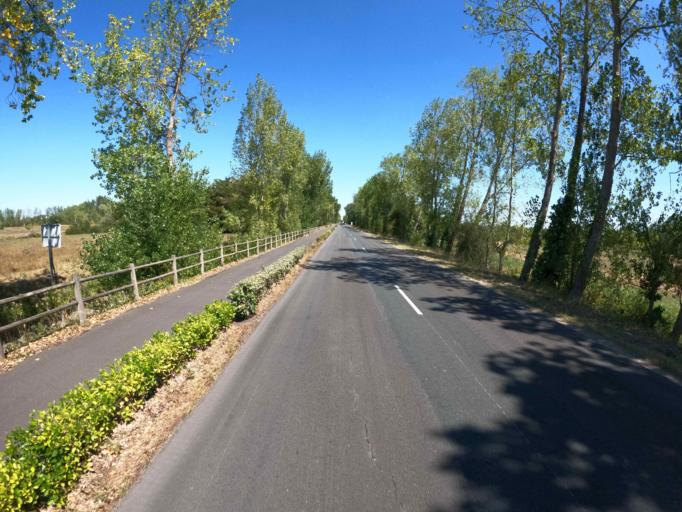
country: FR
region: Pays de la Loire
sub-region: Departement de la Vendee
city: Le Perrier
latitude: 46.8143
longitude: -2.0045
